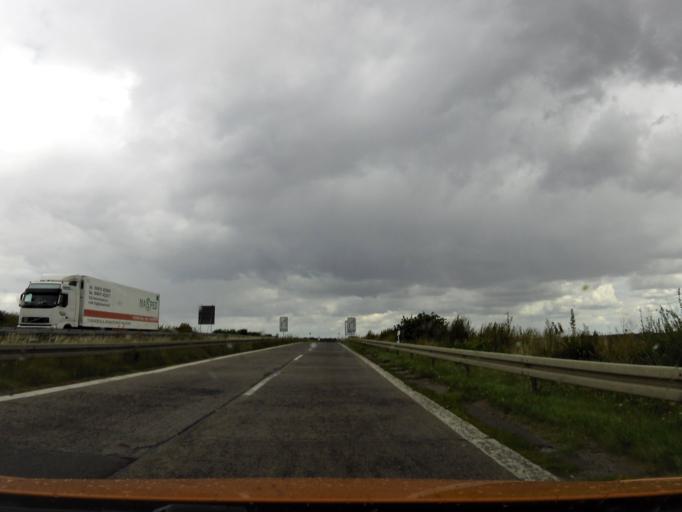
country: DE
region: Brandenburg
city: Zichow
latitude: 53.2873
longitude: 14.0908
